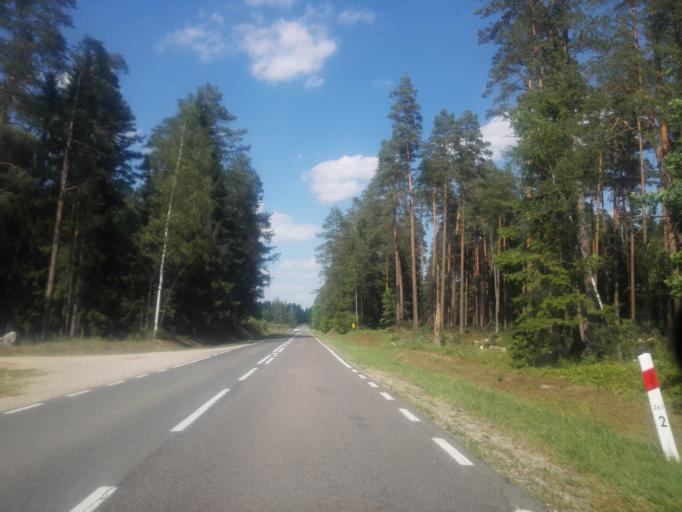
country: PL
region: Podlasie
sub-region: Powiat sejnenski
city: Sejny
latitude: 54.0015
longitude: 23.3165
